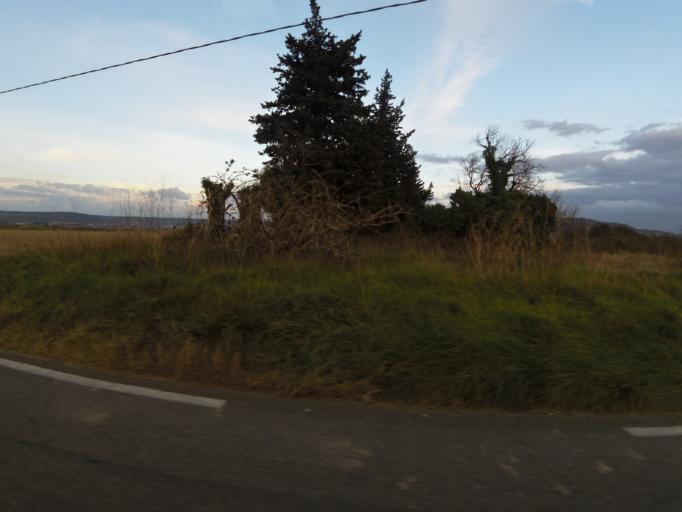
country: FR
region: Languedoc-Roussillon
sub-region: Departement du Gard
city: Calvisson
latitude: 43.7946
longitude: 4.1937
